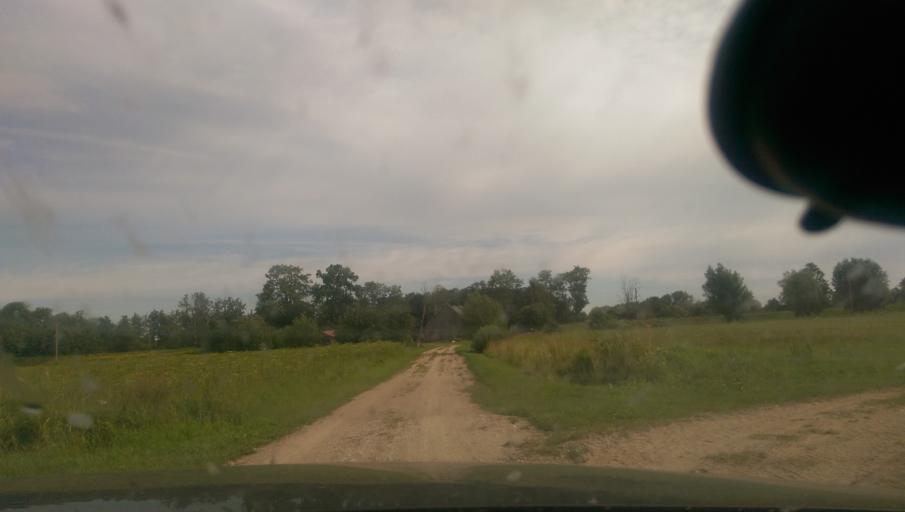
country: LT
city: Rusne
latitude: 55.2963
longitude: 21.3483
